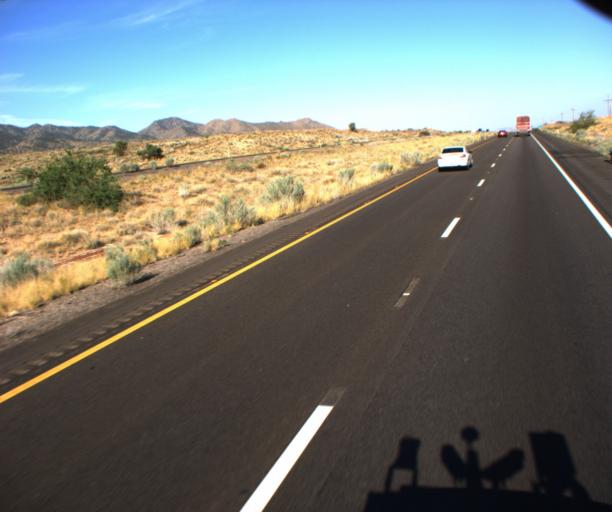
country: US
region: Arizona
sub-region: Mohave County
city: New Kingman-Butler
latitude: 35.1965
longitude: -113.8783
